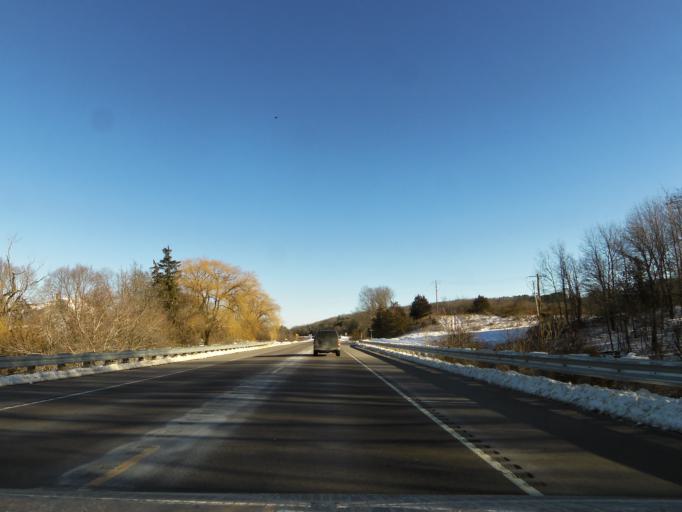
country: US
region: Wisconsin
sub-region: Columbia County
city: Portage
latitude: 43.5079
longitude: -89.5459
